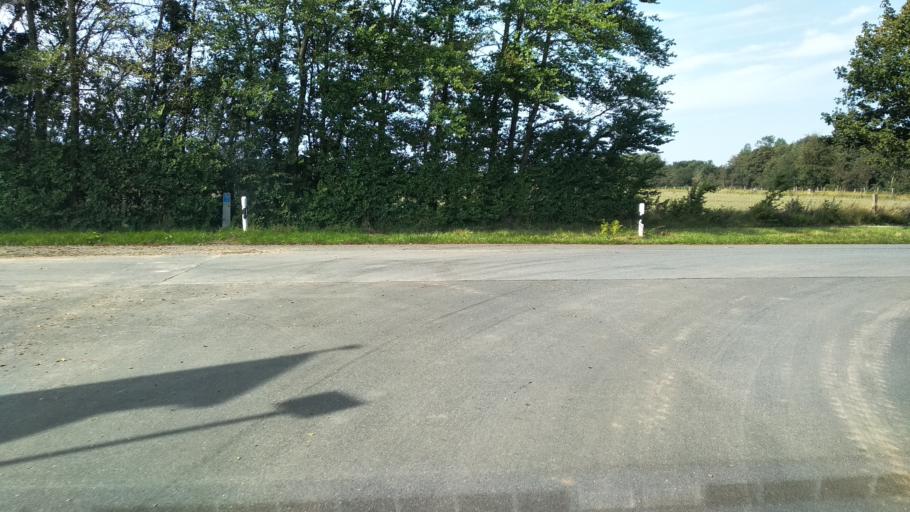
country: DE
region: Schleswig-Holstein
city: Wanderup
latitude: 54.6985
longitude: 9.3275
